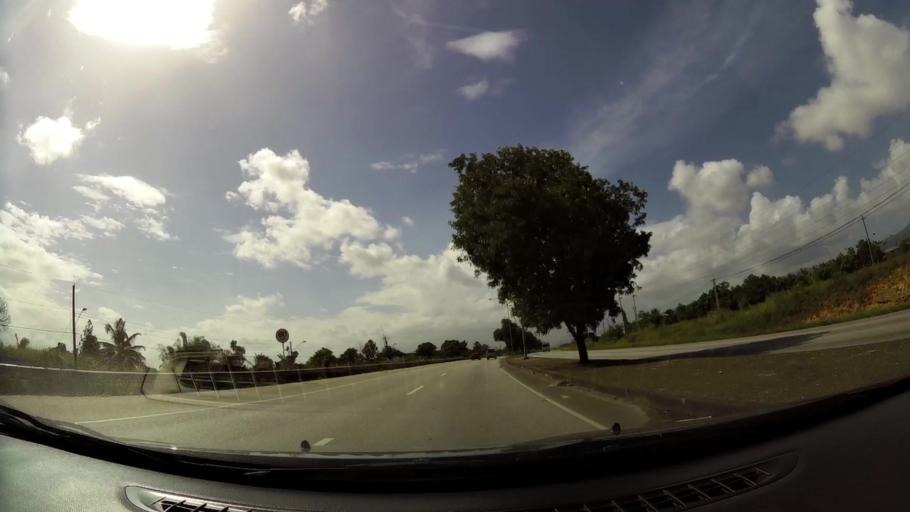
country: TT
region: Borough of Arima
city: Arima
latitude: 10.6068
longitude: -61.2826
